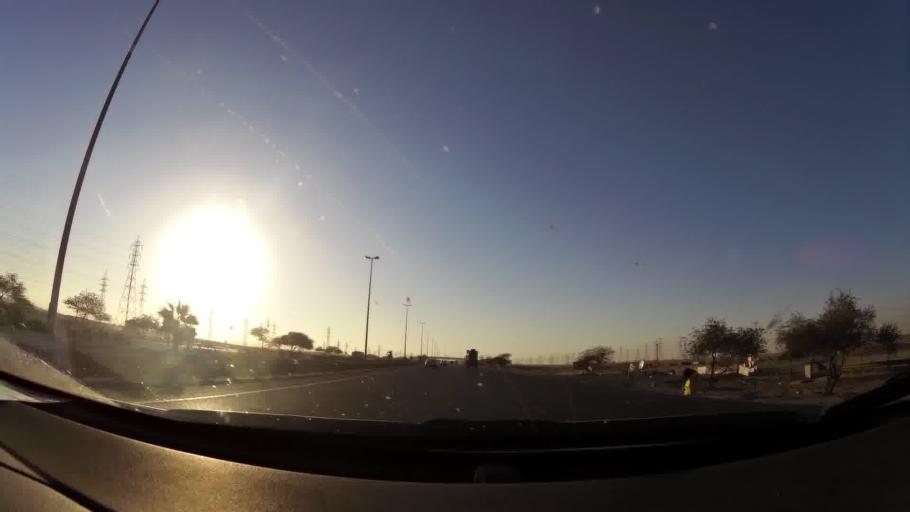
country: KW
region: Al Ahmadi
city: Al Fahahil
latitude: 28.8922
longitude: 48.2229
